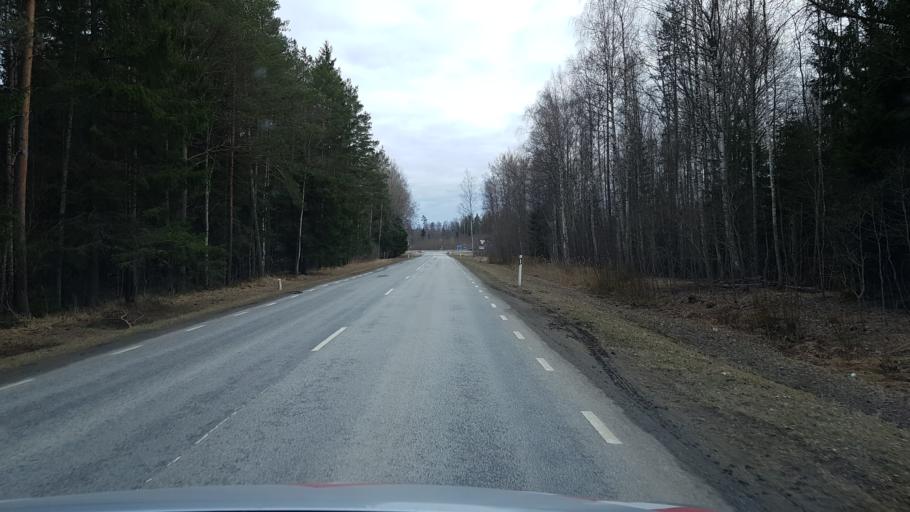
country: EE
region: Ida-Virumaa
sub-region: Toila vald
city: Toila
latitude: 59.3774
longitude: 27.5081
